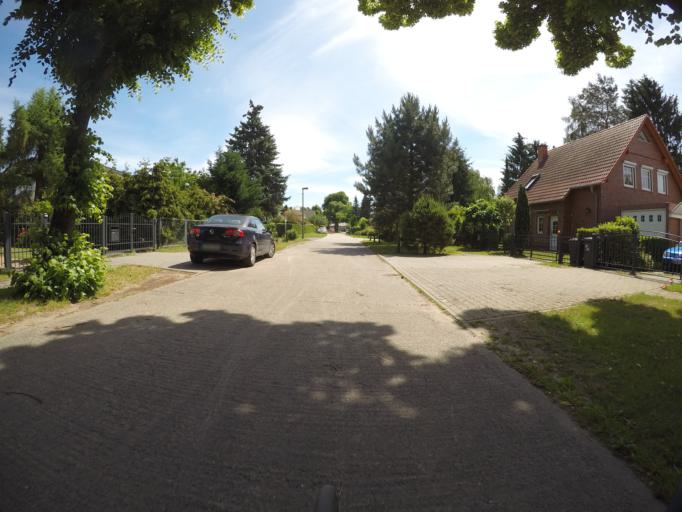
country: DE
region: Berlin
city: Biesdorf
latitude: 52.4971
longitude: 13.5711
